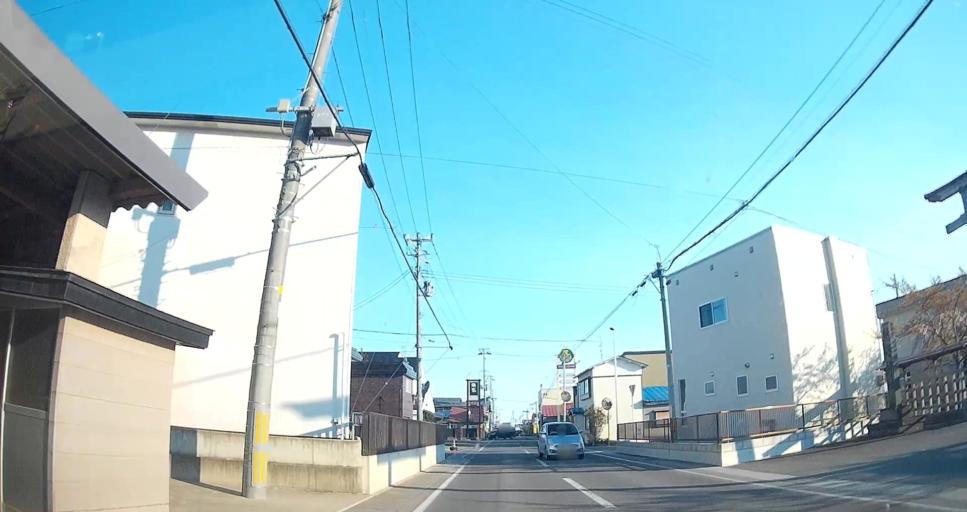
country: JP
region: Aomori
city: Mutsu
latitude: 41.2894
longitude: 141.2111
